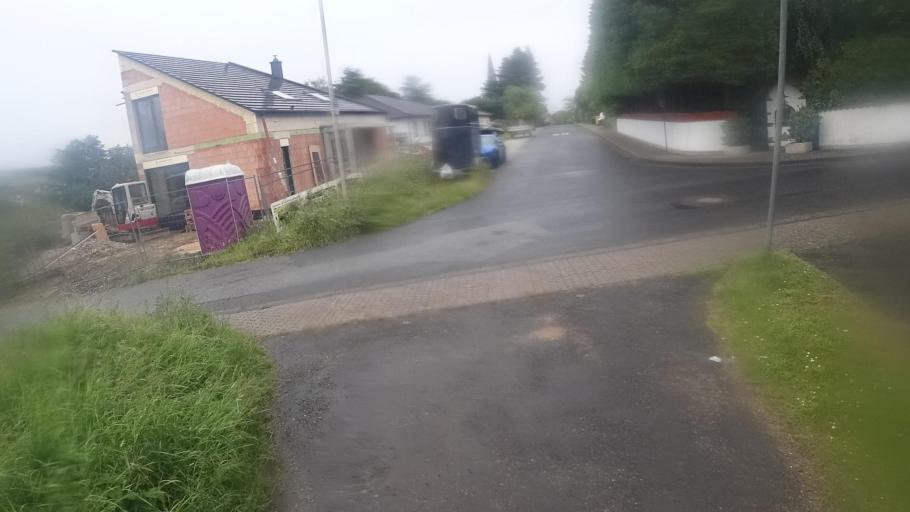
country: DE
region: Rheinland-Pfalz
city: Dernau
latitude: 50.5576
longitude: 7.0525
